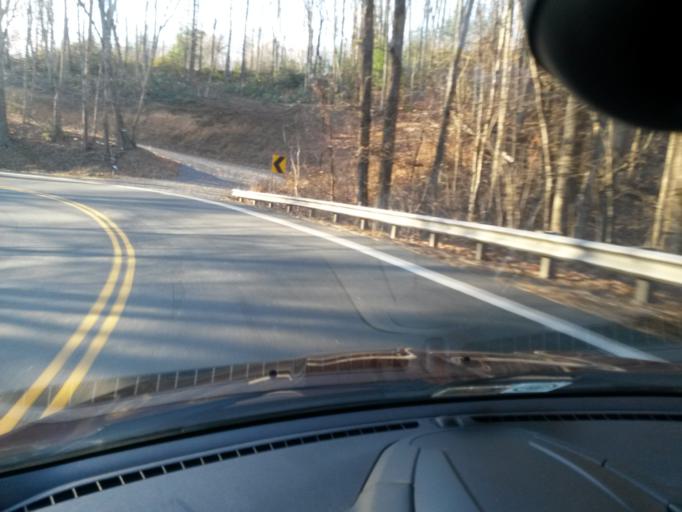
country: US
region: Virginia
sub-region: City of Buena Vista
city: Buena Vista
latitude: 37.7022
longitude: -79.2458
